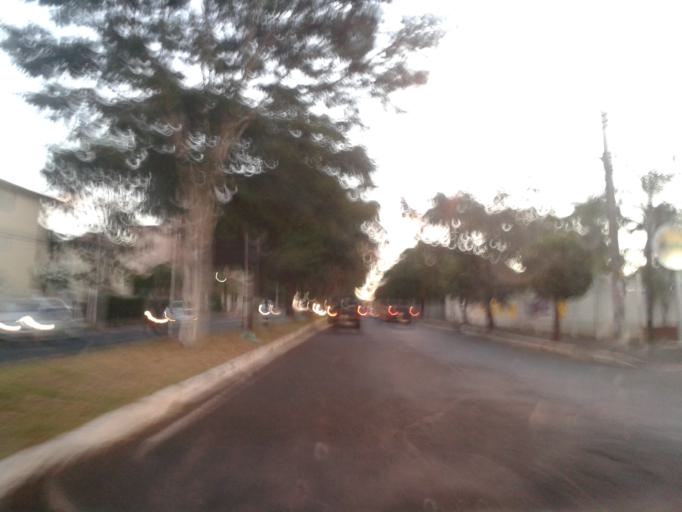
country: BR
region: Minas Gerais
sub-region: Uberlandia
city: Uberlandia
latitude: -18.9283
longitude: -48.2984
